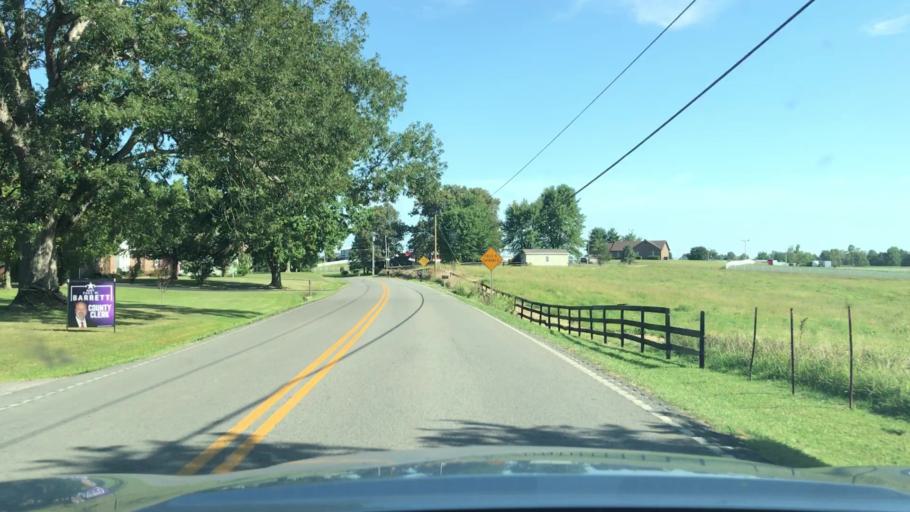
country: US
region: Kentucky
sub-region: Muhlenberg County
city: Greenville
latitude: 37.1619
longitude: -87.1428
